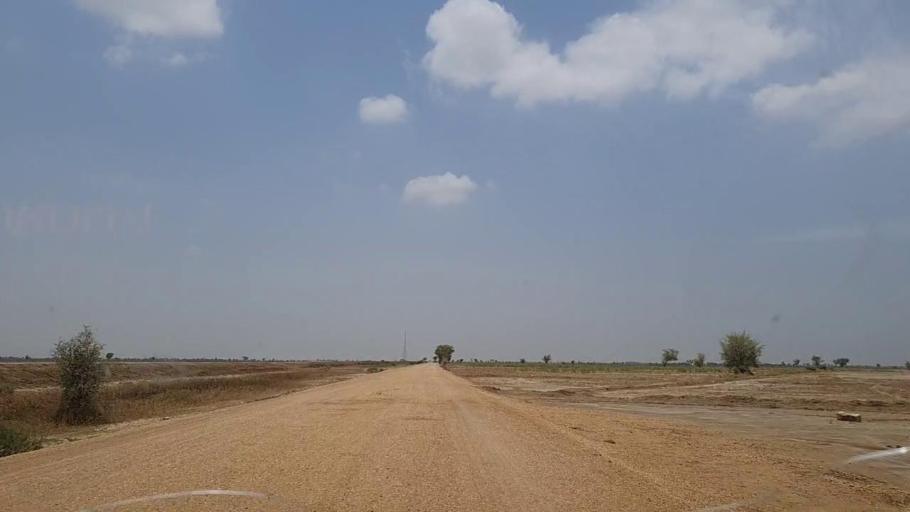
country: PK
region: Sindh
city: Johi
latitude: 26.7741
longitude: 67.6547
